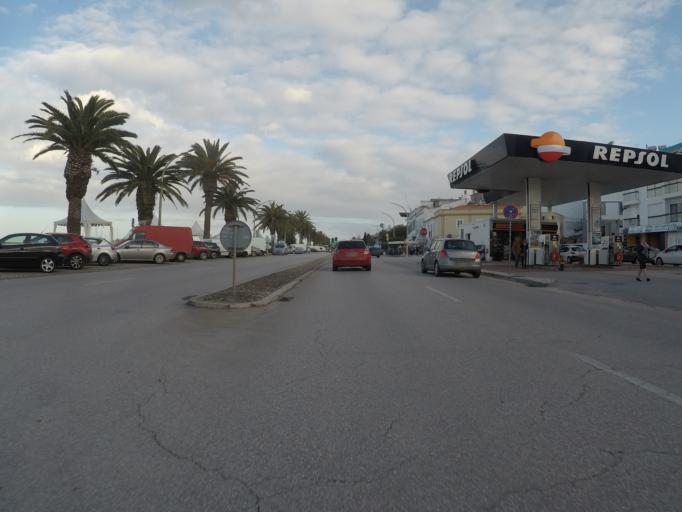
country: PT
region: Faro
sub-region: Lagos
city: Lagos
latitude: 37.1052
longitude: -8.6736
